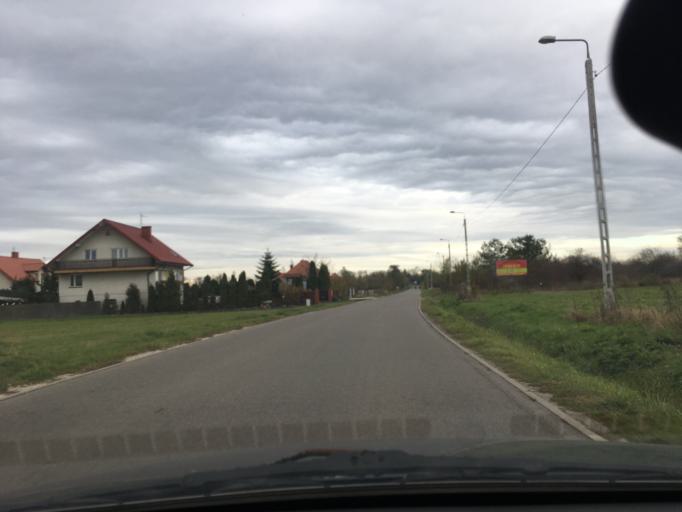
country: PL
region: Lodz Voivodeship
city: Zabia Wola
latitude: 52.0104
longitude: 20.6964
